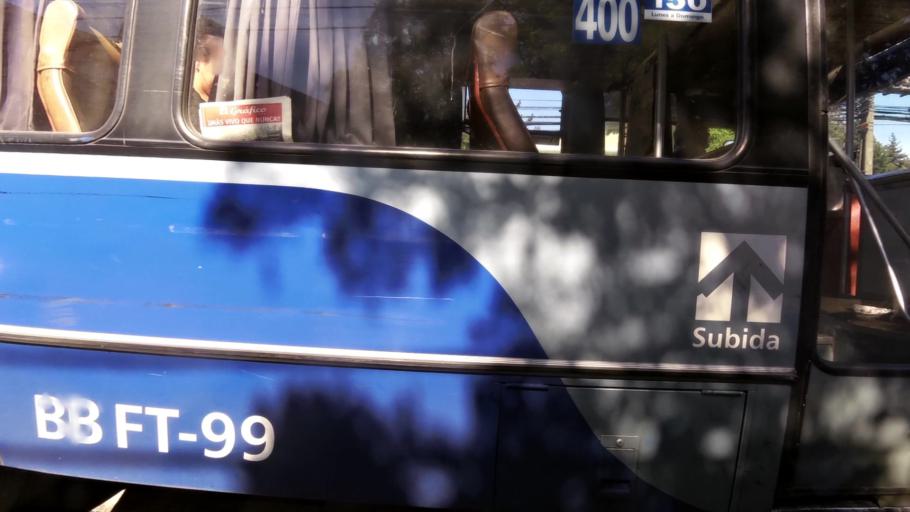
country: CL
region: Biobio
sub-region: Provincia de Concepcion
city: Concepcion
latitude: -36.8217
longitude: -73.0360
